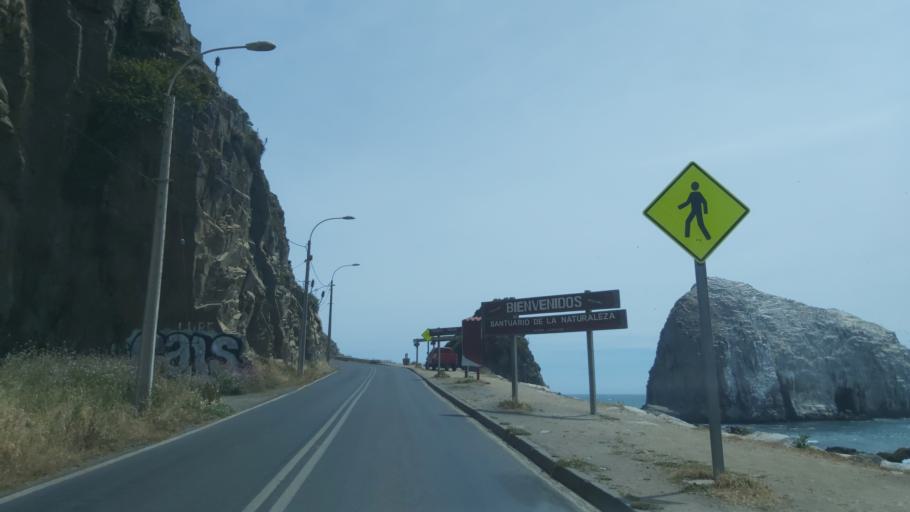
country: CL
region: Maule
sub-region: Provincia de Talca
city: Constitucion
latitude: -35.3283
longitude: -72.4308
